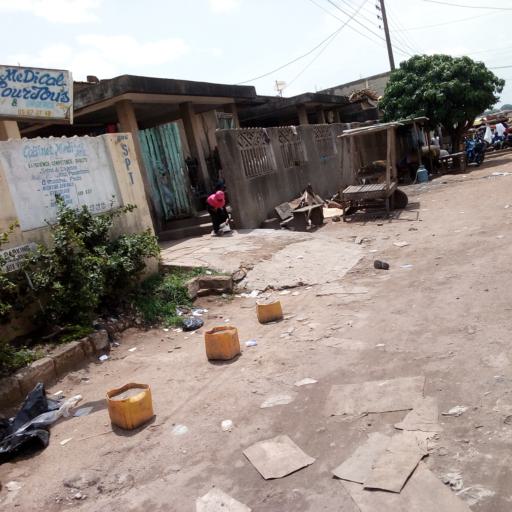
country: CI
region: Vallee du Bandama
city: Bouake
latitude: 7.6916
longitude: -5.0249
